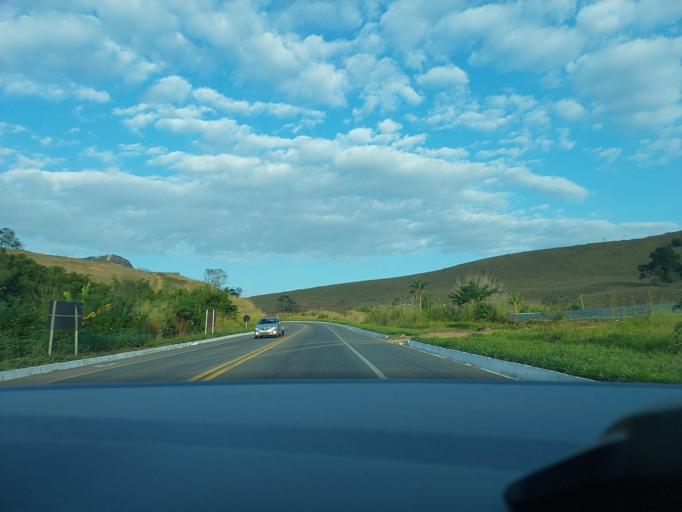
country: BR
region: Minas Gerais
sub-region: Muriae
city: Muriae
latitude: -21.1273
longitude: -42.3266
